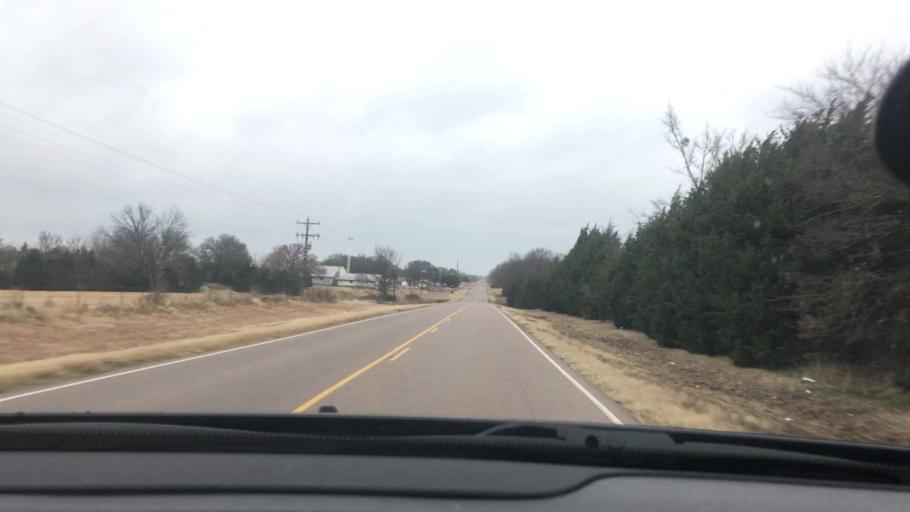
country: US
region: Oklahoma
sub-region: Johnston County
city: Tishomingo
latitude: 34.2780
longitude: -96.6711
